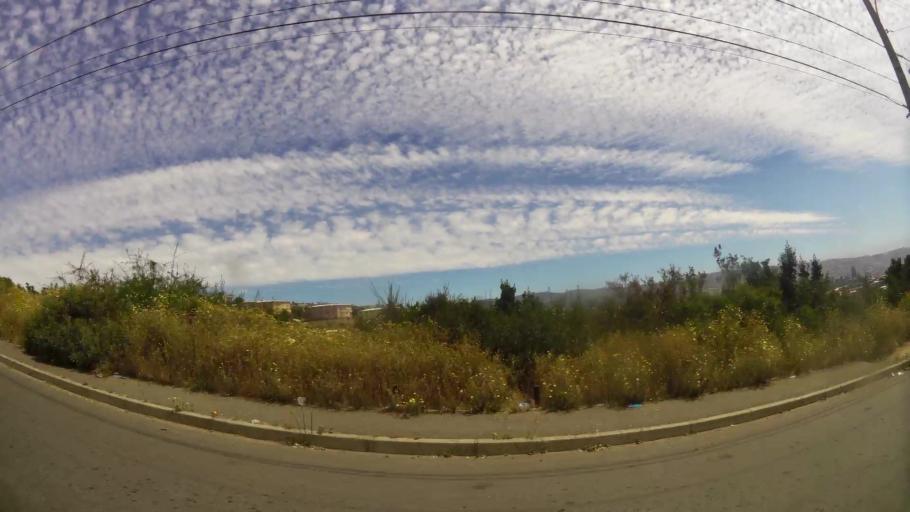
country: CL
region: Valparaiso
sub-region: Provincia de Valparaiso
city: Vina del Mar
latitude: -33.0559
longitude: -71.5697
